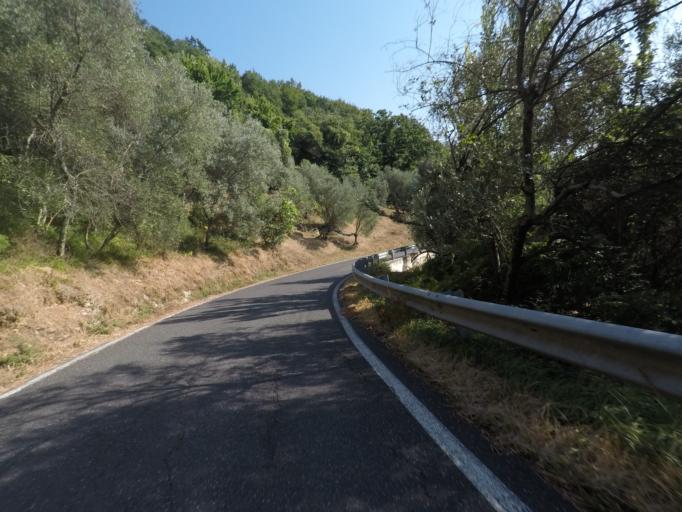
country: IT
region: Liguria
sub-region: Provincia di La Spezia
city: Casano-Dogana-Isola
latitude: 44.0830
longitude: 10.0504
